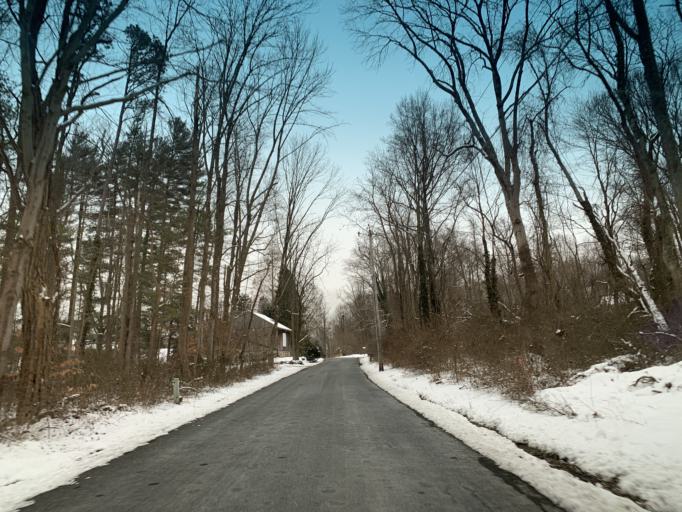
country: US
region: Maryland
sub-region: Harford County
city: Aberdeen
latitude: 39.5613
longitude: -76.1826
